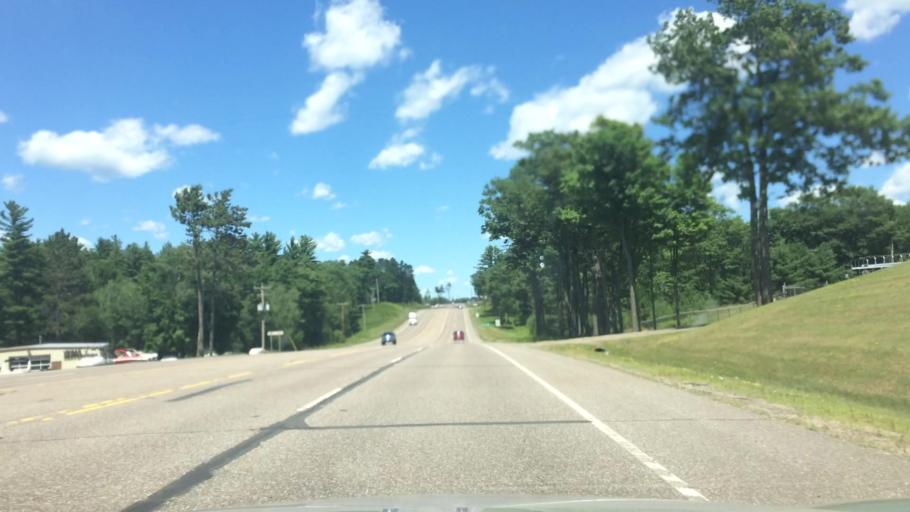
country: US
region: Wisconsin
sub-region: Vilas County
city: Lac du Flambeau
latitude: 45.8448
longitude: -89.7056
